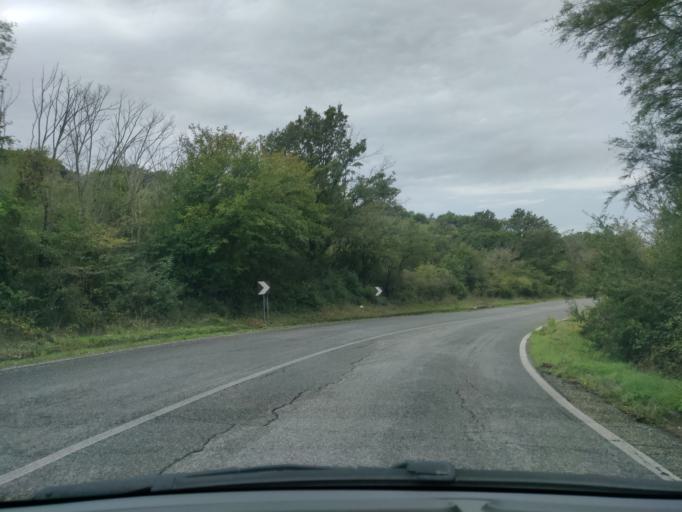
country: IT
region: Latium
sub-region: Citta metropolitana di Roma Capitale
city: Civitavecchia
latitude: 42.1116
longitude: 11.8518
